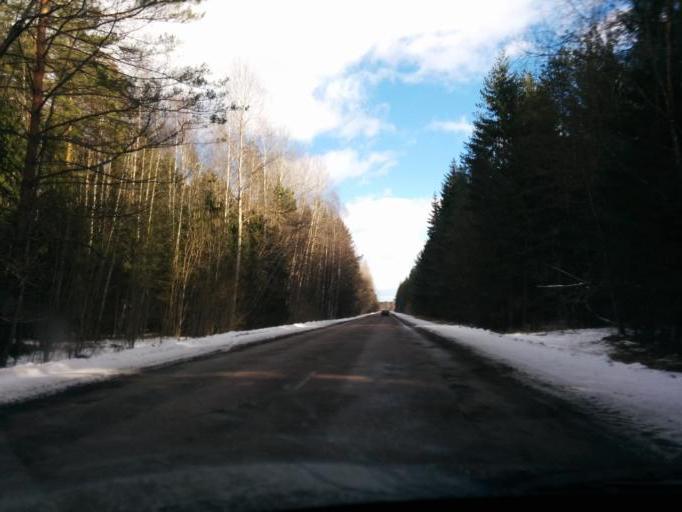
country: LV
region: Gulbenes Rajons
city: Gulbene
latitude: 57.1921
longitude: 26.9350
